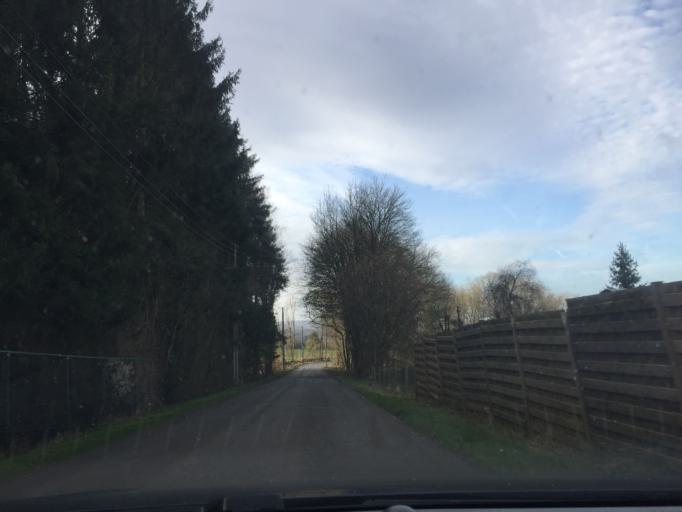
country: BE
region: Wallonia
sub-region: Province du Luxembourg
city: Hotton
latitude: 50.2939
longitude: 5.4885
